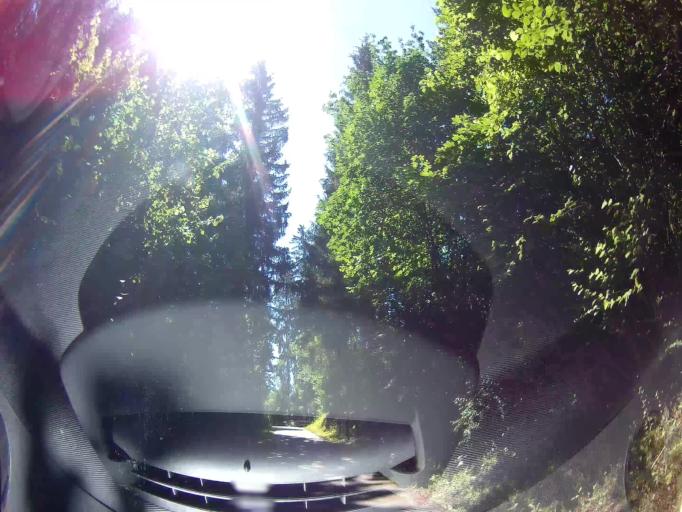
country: AT
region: Carinthia
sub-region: Politischer Bezirk Spittal an der Drau
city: Lendorf
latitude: 46.8217
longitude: 13.4433
